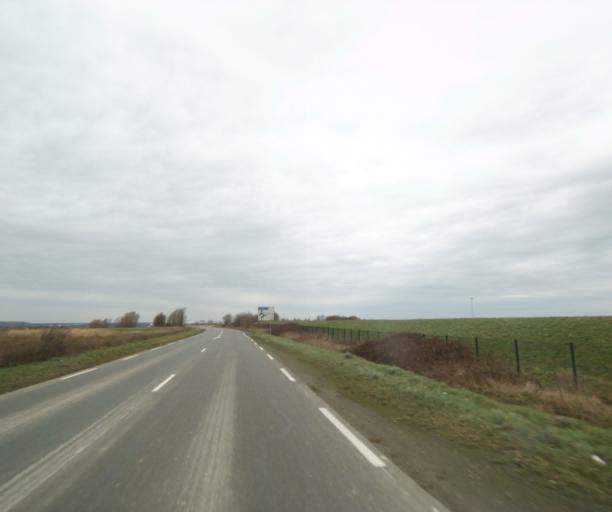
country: FR
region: Nord-Pas-de-Calais
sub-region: Departement du Nord
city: Onnaing
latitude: 50.3604
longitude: 3.6103
